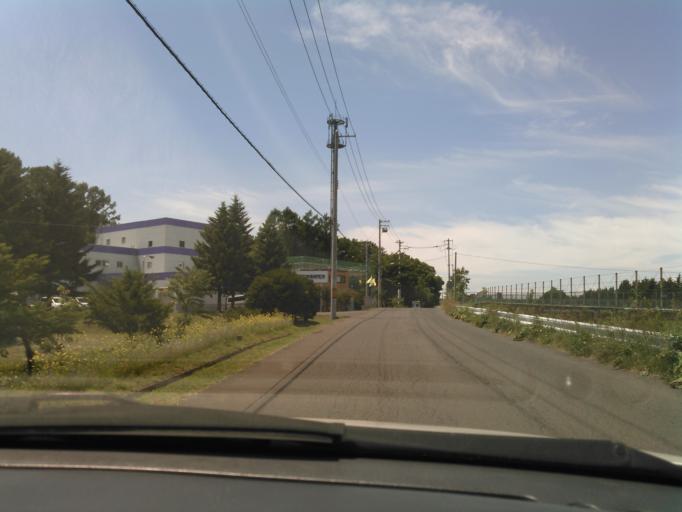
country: JP
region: Hokkaido
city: Ebetsu
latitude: 43.0800
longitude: 141.5312
